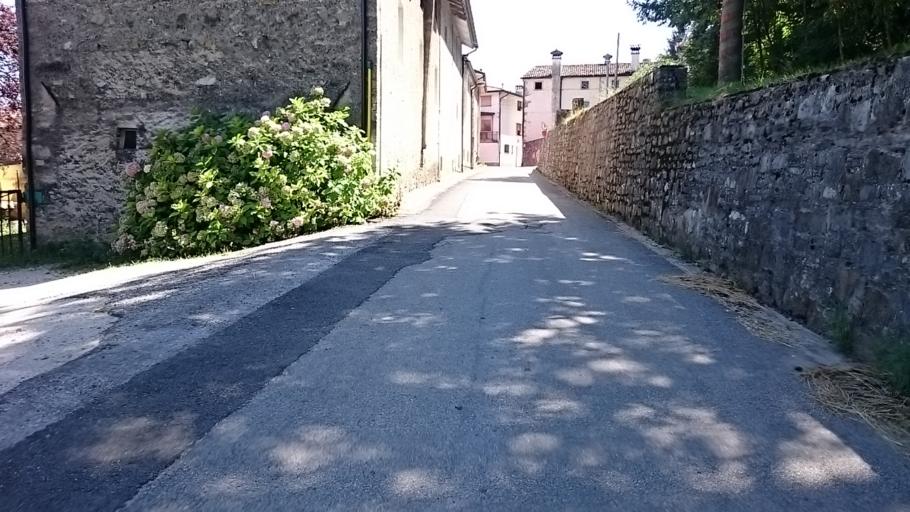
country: IT
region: Veneto
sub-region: Provincia di Treviso
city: Follina
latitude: 45.9391
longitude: 12.1260
